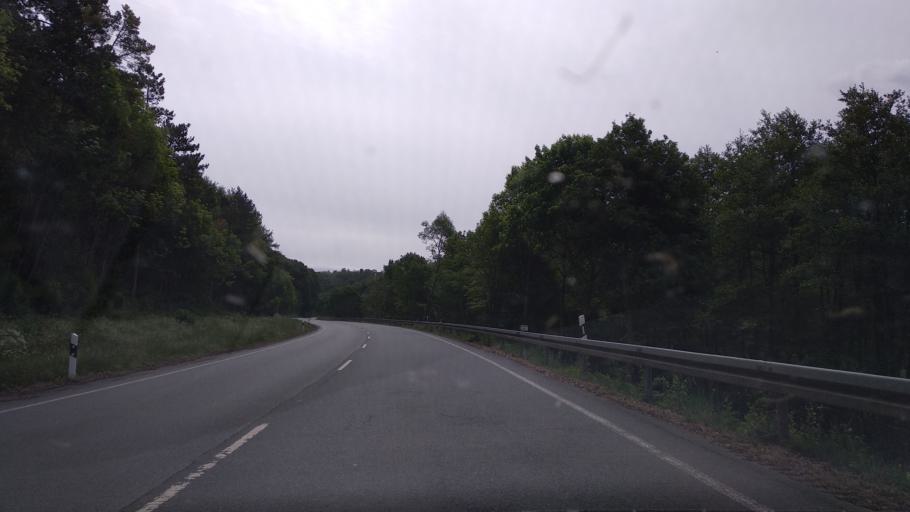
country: DE
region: North Rhine-Westphalia
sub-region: Regierungsbezirk Detmold
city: Willebadessen
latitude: 51.6270
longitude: 9.0835
